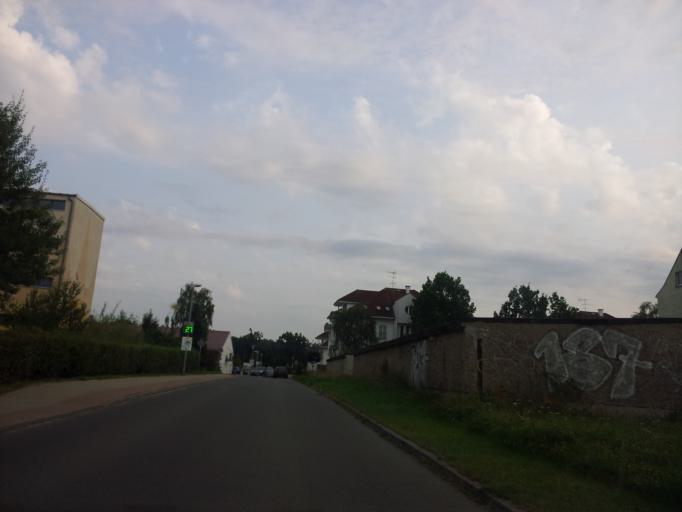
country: DE
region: Brandenburg
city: Treuenbrietzen
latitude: 52.0891
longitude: 12.8480
